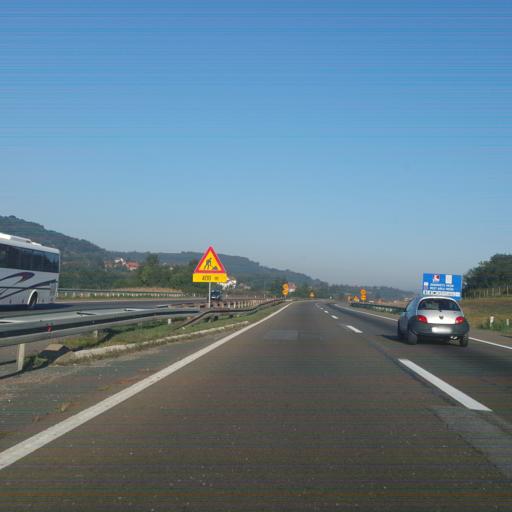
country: RS
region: Central Serbia
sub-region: Belgrade
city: Grocka
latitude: 44.6579
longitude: 20.6207
